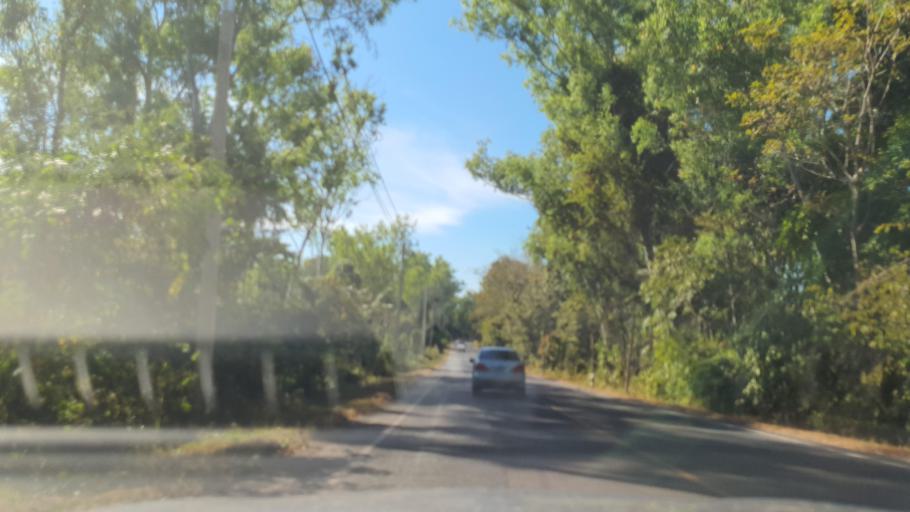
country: TH
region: Kalasin
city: Khao Wong
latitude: 16.7643
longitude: 104.1447
